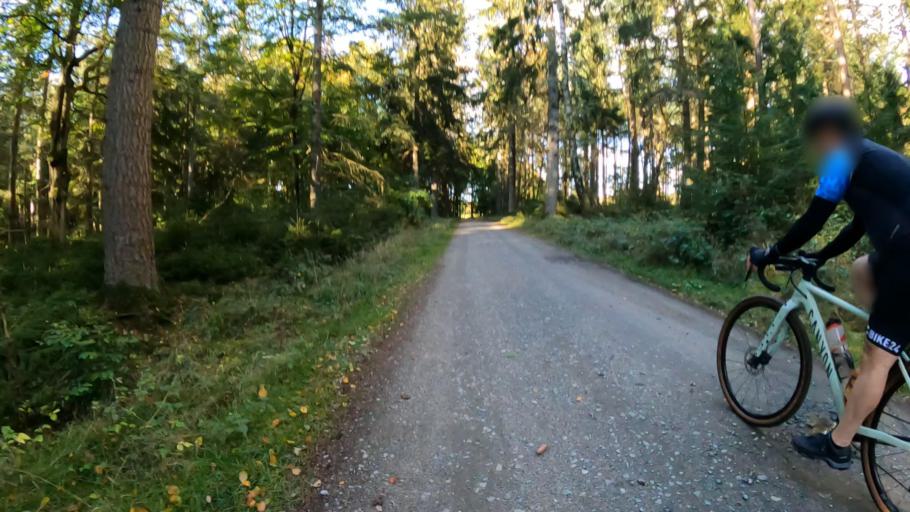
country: DE
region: Schleswig-Holstein
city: Heidmuhlen
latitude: 53.9508
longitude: 10.1233
